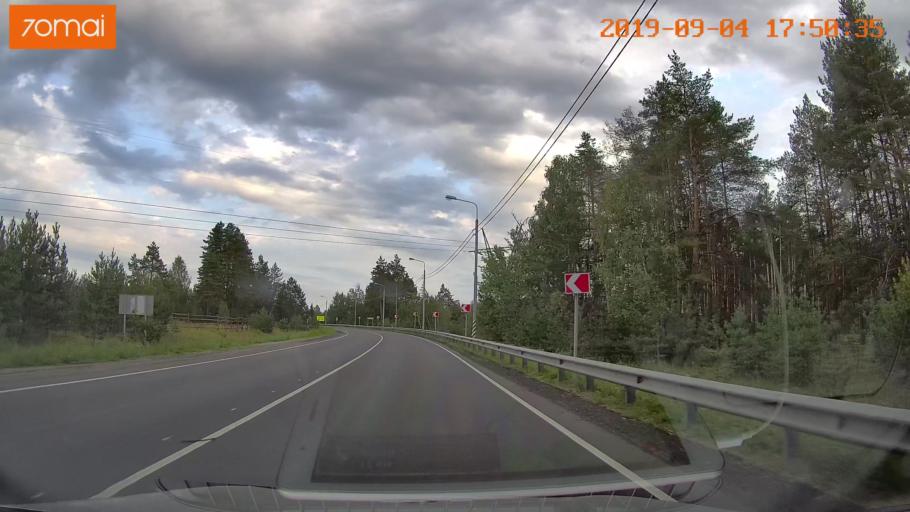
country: RU
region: Moskovskaya
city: Imeni Tsyurupy
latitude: 55.5246
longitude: 38.6843
